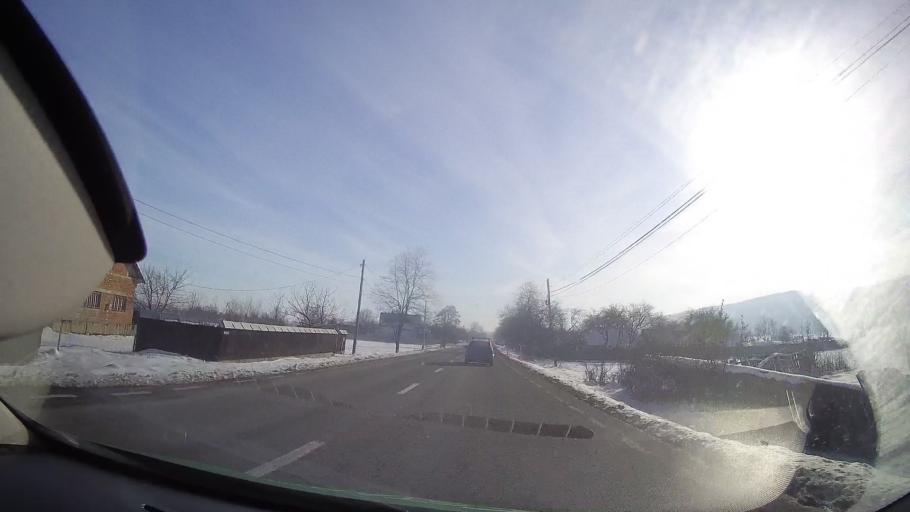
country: RO
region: Neamt
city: Bodesti
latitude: 47.0457
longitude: 26.4049
